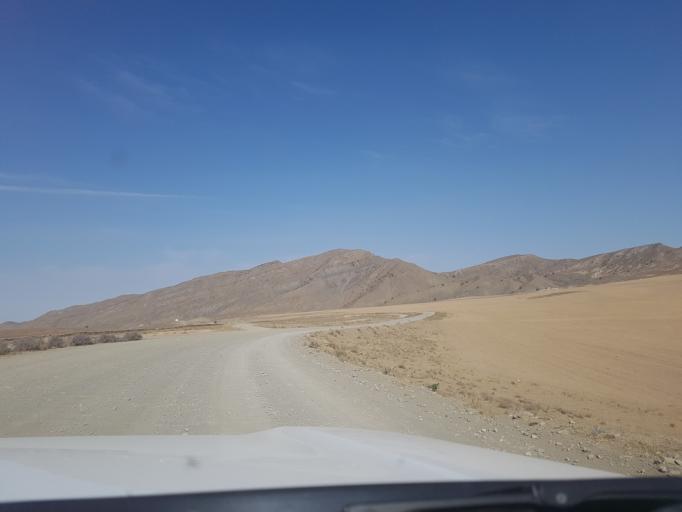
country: TM
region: Ahal
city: Baharly
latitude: 38.4335
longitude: 57.0353
